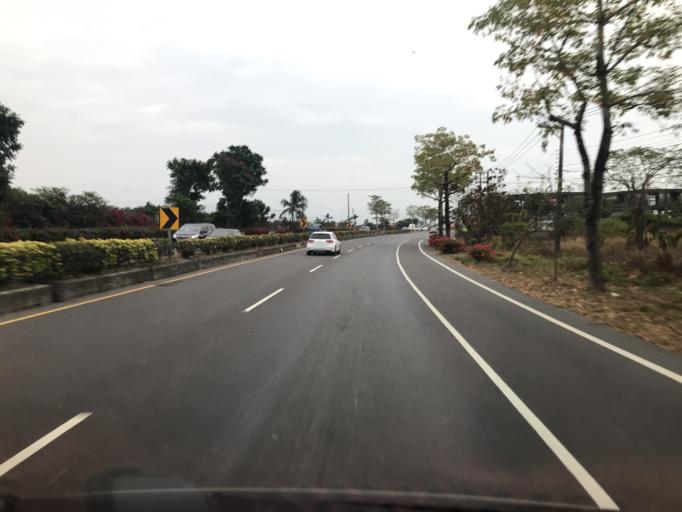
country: TW
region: Taiwan
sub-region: Pingtung
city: Pingtung
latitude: 22.4207
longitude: 120.5825
